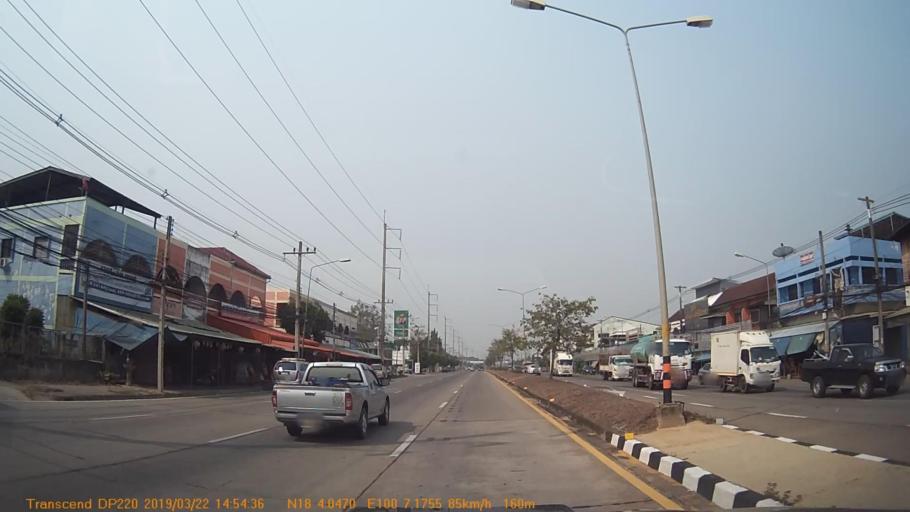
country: TH
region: Phrae
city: Sung Men
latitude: 18.0678
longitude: 100.1197
